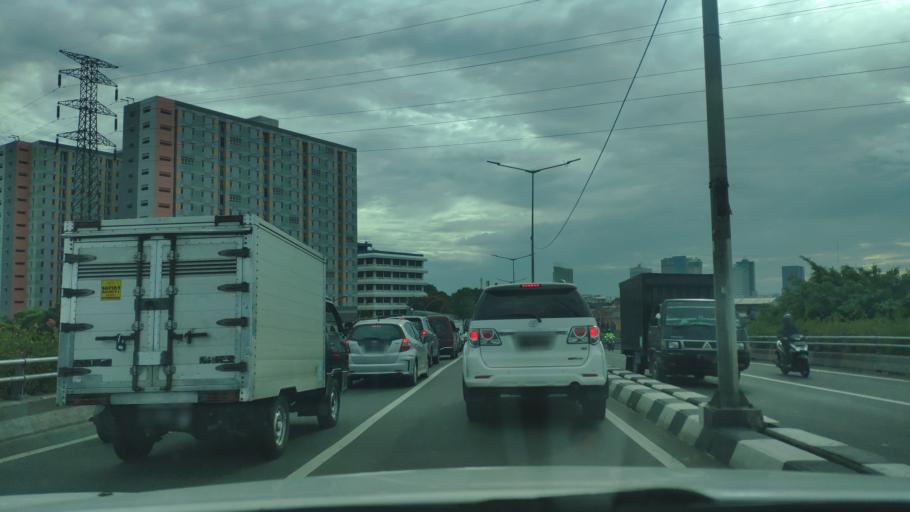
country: ID
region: Jakarta Raya
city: Jakarta
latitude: -6.1850
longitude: 106.8104
